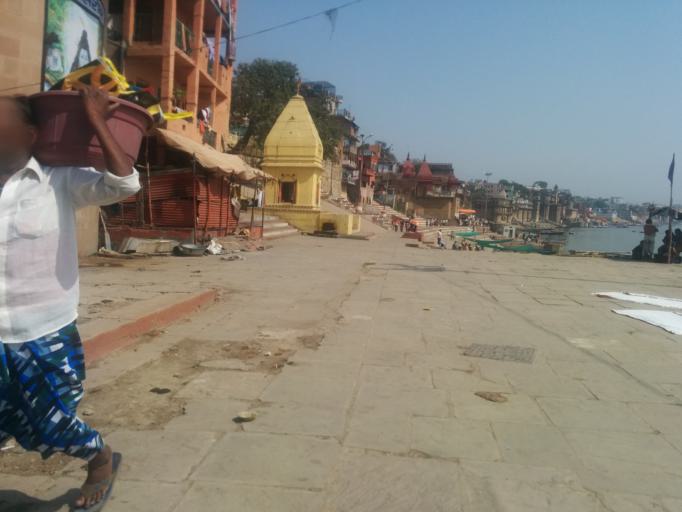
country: IN
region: Uttar Pradesh
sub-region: Varanasi
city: Varanasi
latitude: 25.3010
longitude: 83.0076
